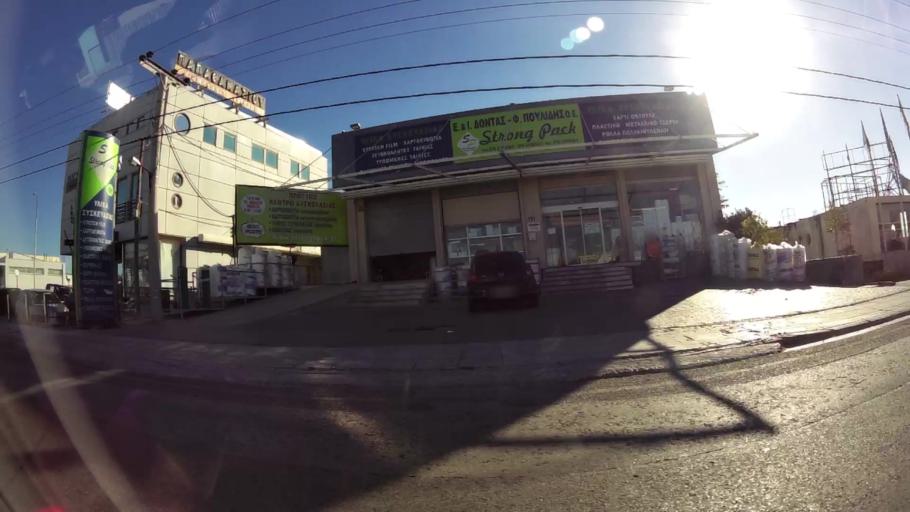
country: GR
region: Attica
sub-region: Nomarchia Athinas
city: Metamorfosi
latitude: 38.0842
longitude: 23.7639
